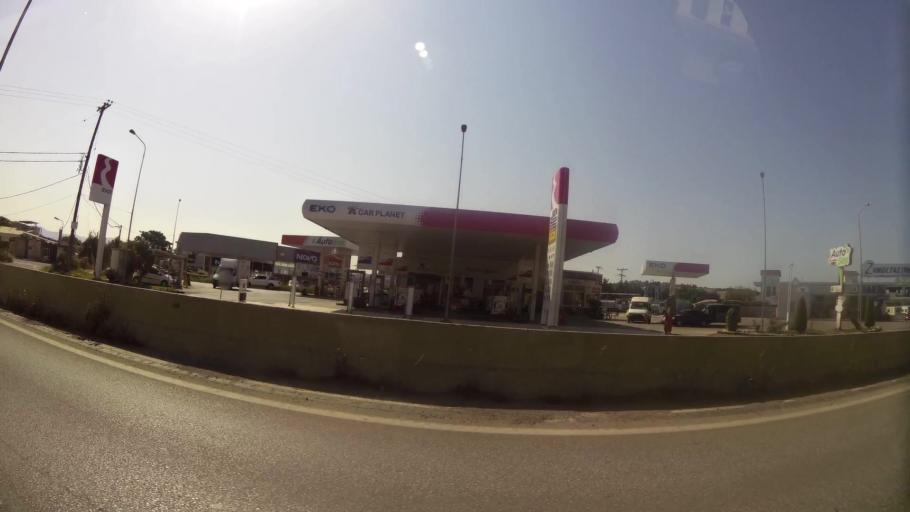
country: GR
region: Central Macedonia
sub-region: Nomos Thessalonikis
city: Neo Rysi
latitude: 40.5034
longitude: 22.9709
